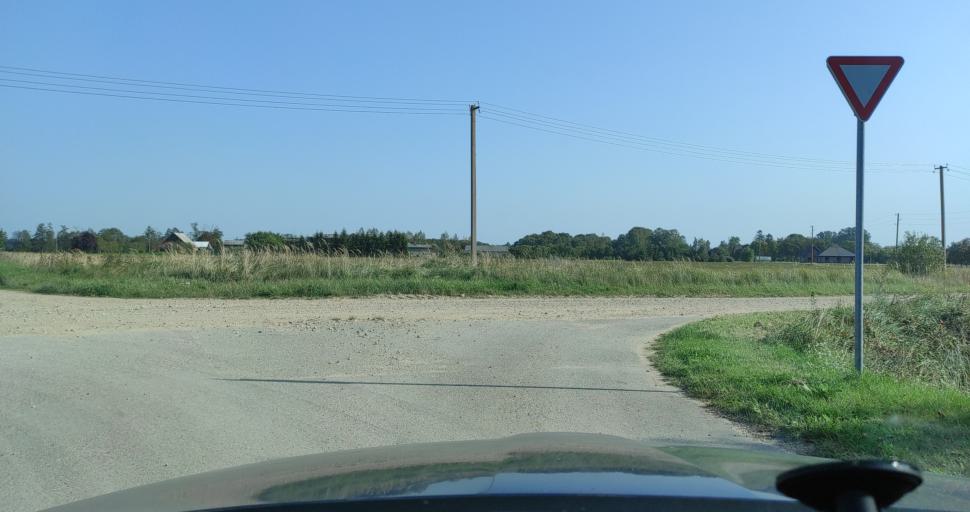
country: LV
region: Ventspils Rajons
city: Piltene
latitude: 57.2310
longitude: 21.6135
